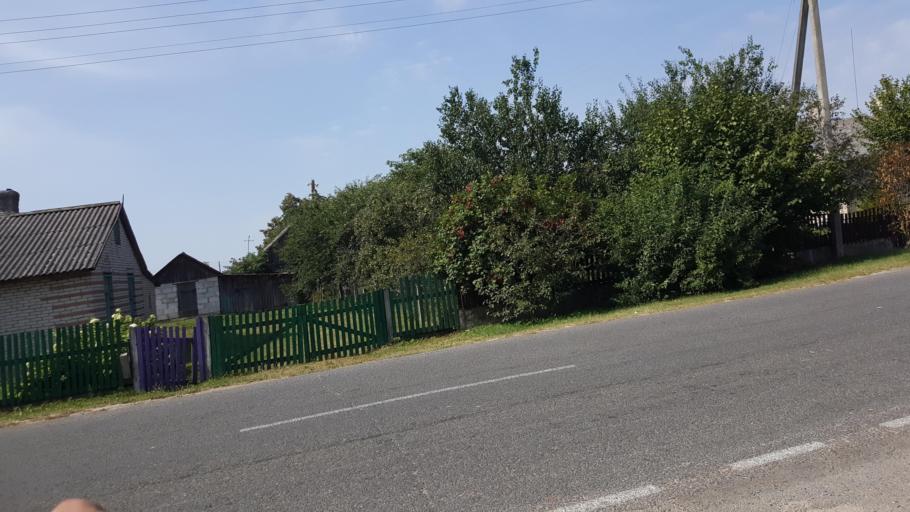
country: BY
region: Brest
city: Kamyanyets
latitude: 52.4657
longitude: 23.7334
